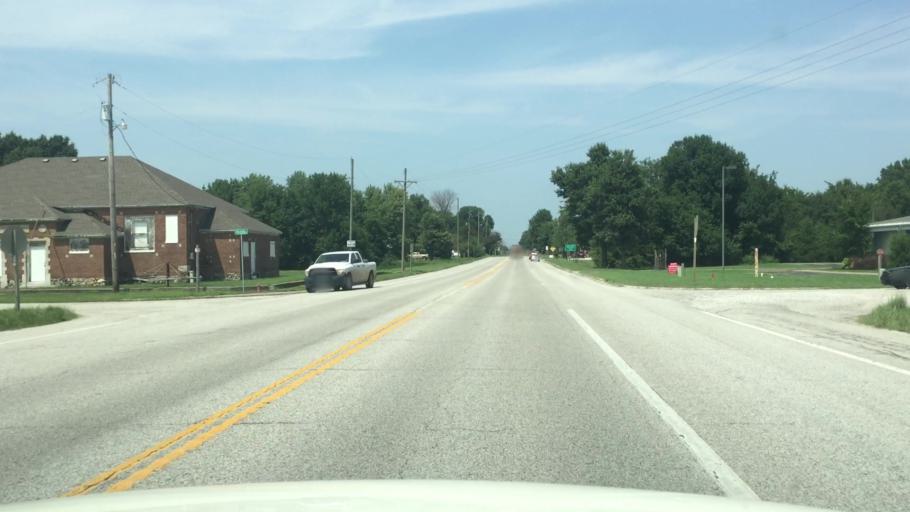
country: US
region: Kansas
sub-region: Cherokee County
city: Galena
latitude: 37.1630
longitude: -94.7043
